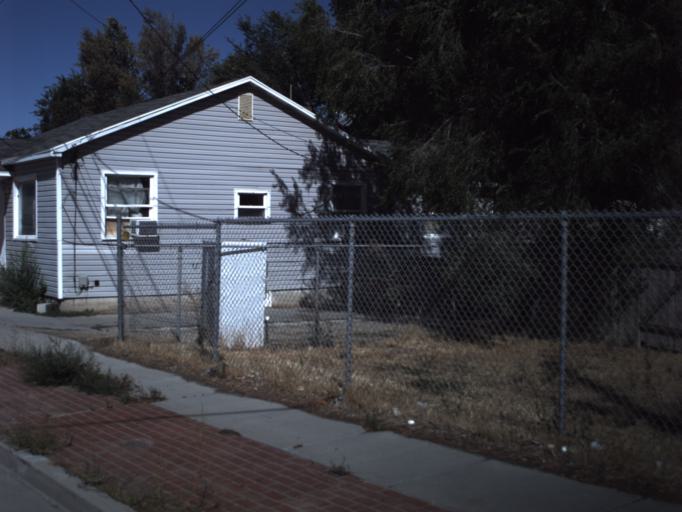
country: US
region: Utah
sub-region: Salt Lake County
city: West Jordan
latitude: 40.5952
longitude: -111.9386
